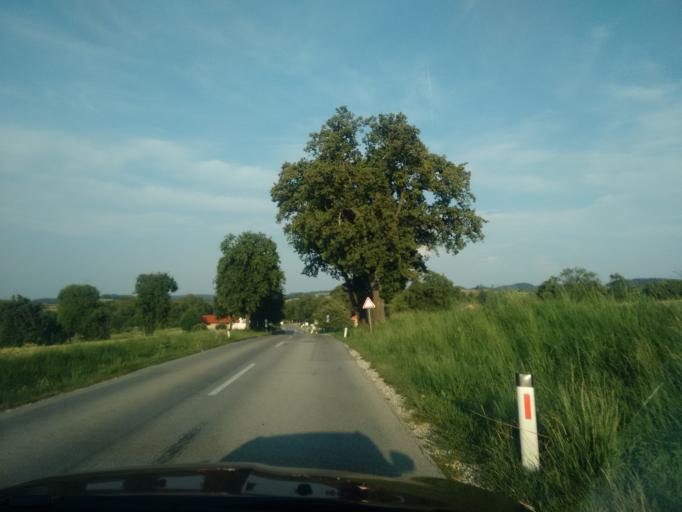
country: AT
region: Upper Austria
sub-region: Politischer Bezirk Vocklabruck
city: Wolfsegg am Hausruck
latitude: 48.1461
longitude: 13.6875
